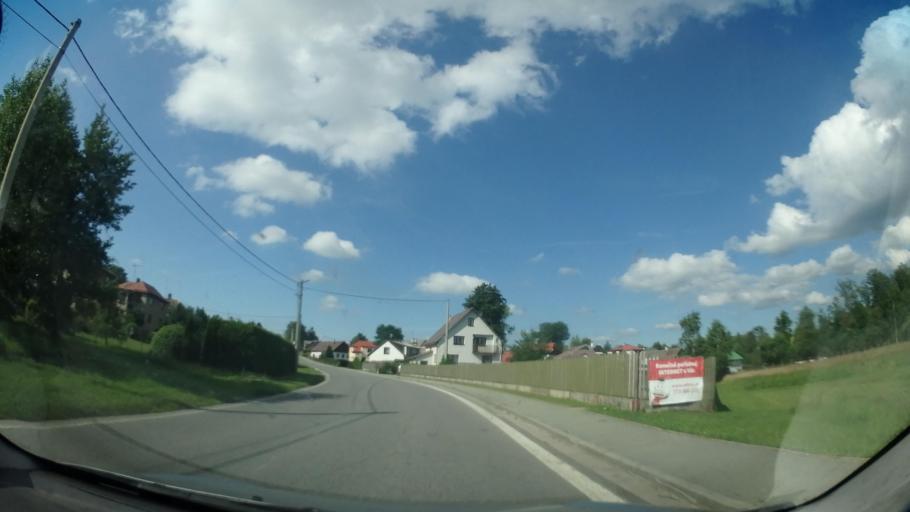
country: CZ
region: Vysocina
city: Heralec
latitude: 49.6921
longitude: 15.9927
